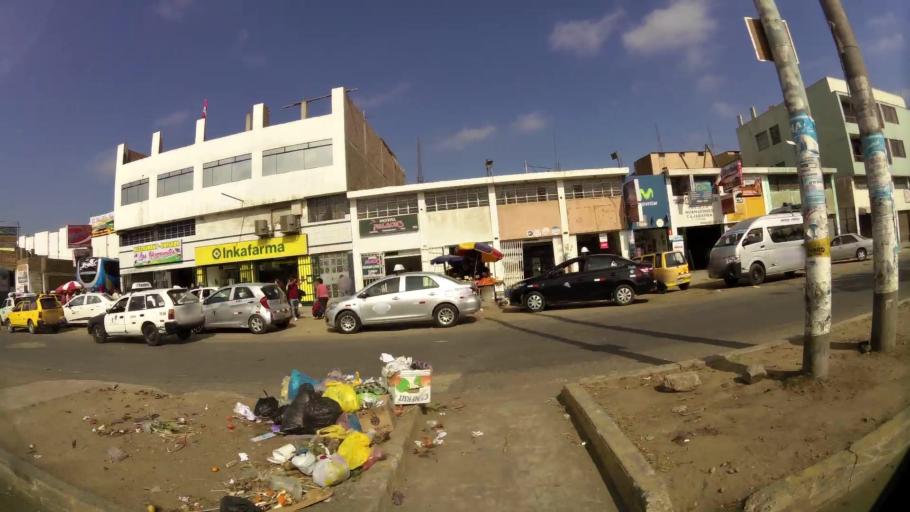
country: PE
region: La Libertad
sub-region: Provincia de Trujillo
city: El Porvenir
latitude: -8.1017
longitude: -79.0102
